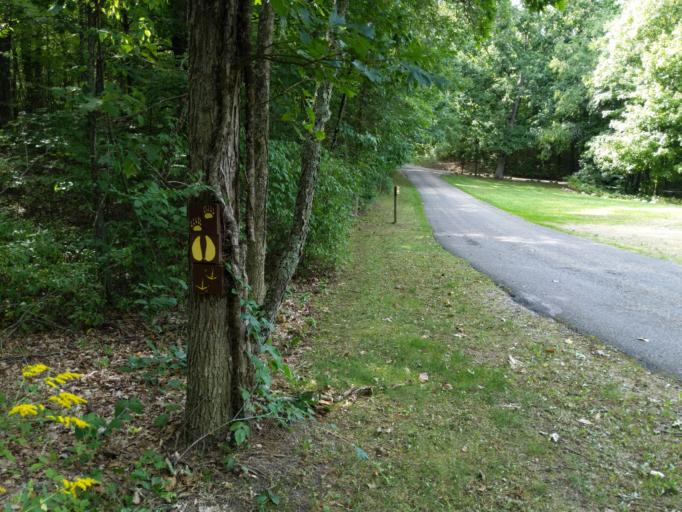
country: US
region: Michigan
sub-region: Ionia County
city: Ionia
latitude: 42.9729
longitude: -85.1207
